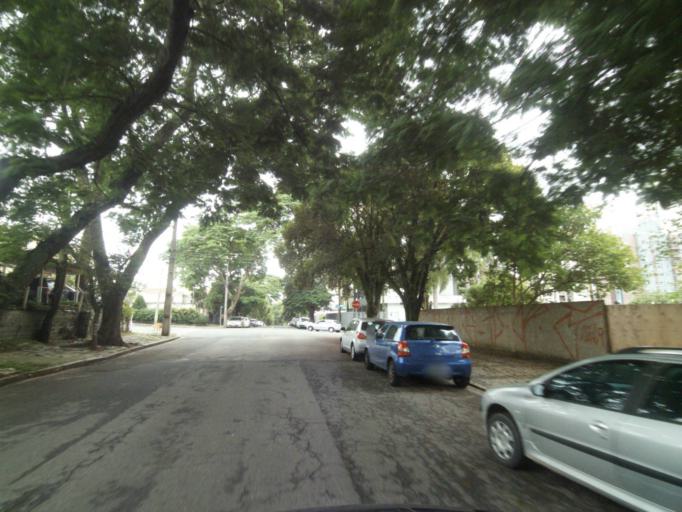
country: BR
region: Parana
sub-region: Curitiba
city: Curitiba
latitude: -25.4150
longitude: -49.2628
